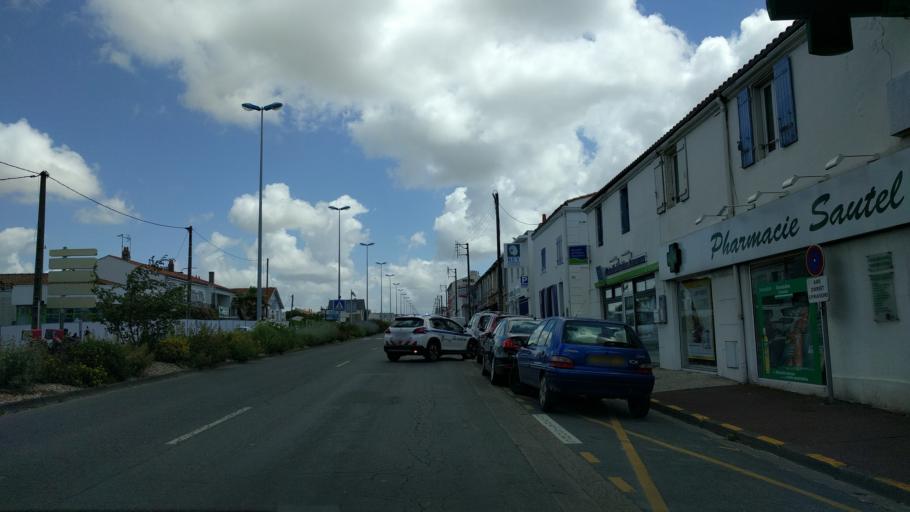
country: FR
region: Poitou-Charentes
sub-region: Departement de la Charente-Maritime
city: La Rochelle
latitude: 46.1670
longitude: -1.1355
